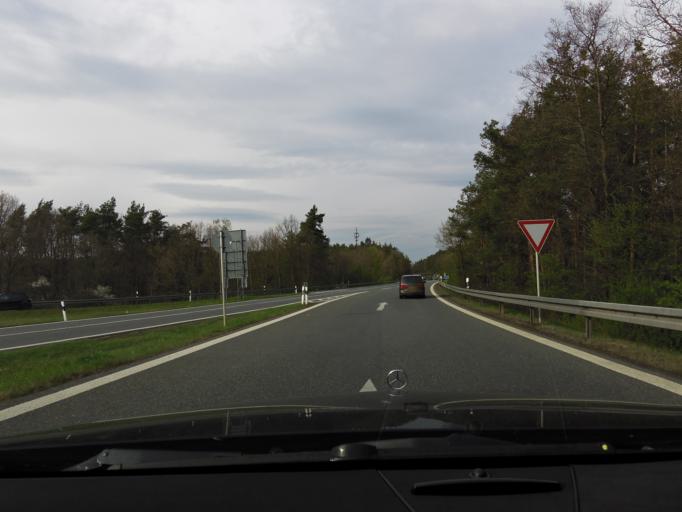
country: DE
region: Bavaria
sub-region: Regierungsbezirk Mittelfranken
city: Hochstadt an der Aisch
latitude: 49.7277
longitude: 10.8229
